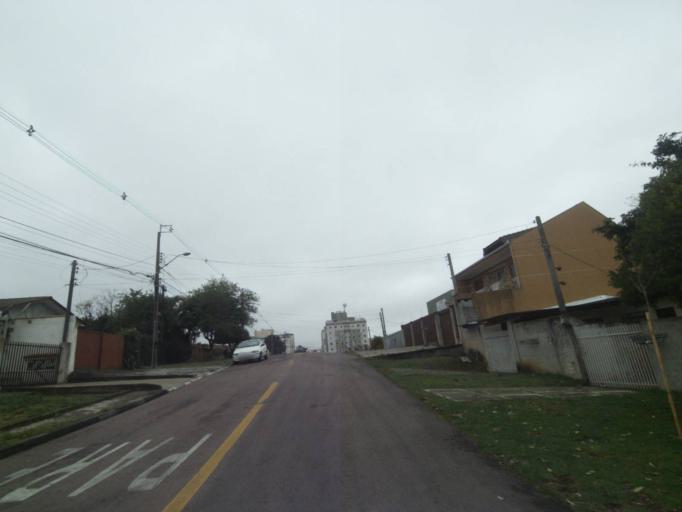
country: BR
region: Parana
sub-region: Curitiba
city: Curitiba
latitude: -25.5042
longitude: -49.3010
